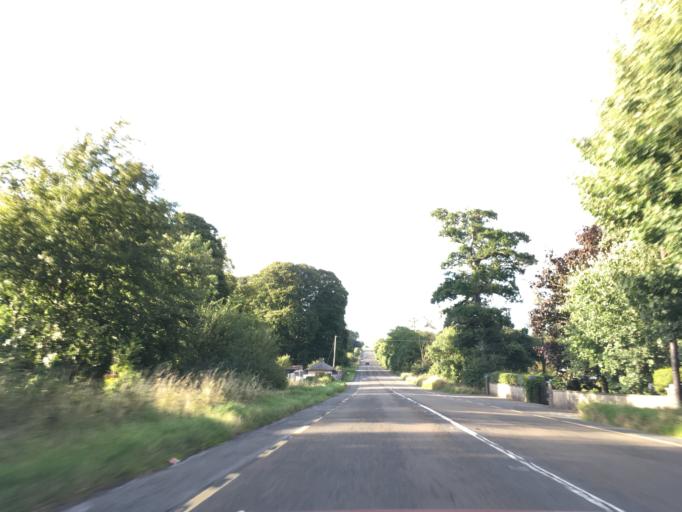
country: IE
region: Munster
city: Cashel
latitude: 52.4831
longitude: -7.8917
